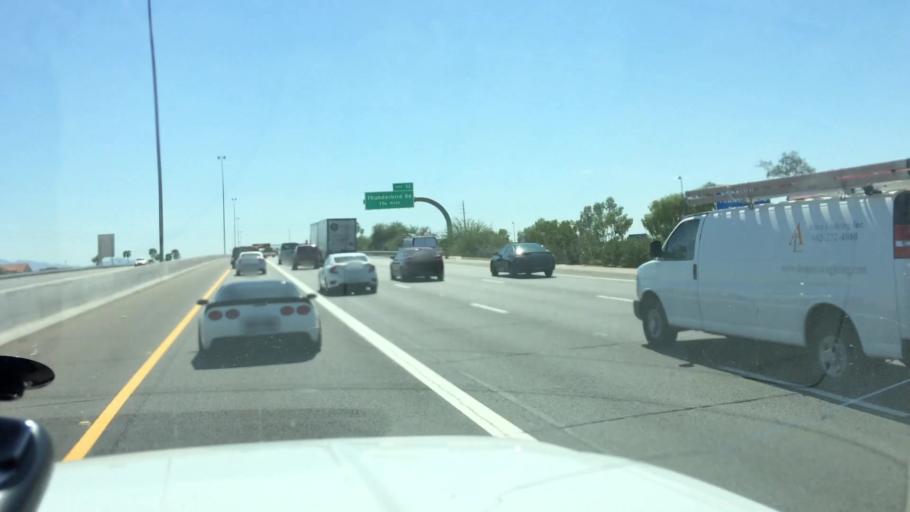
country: US
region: Arizona
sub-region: Maricopa County
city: Sun City
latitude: 33.6425
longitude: -112.2372
